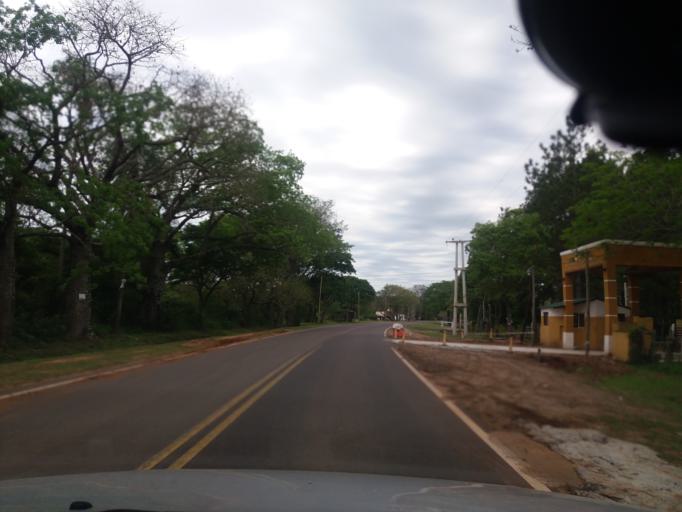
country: AR
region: Corrientes
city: San Luis del Palmar
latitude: -27.4569
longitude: -58.6772
